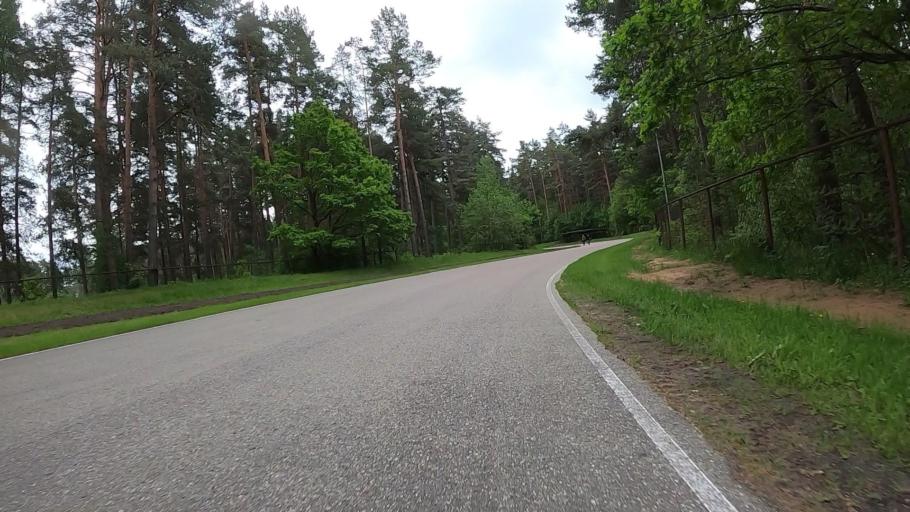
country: LV
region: Stopini
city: Ulbroka
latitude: 56.9668
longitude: 24.2194
